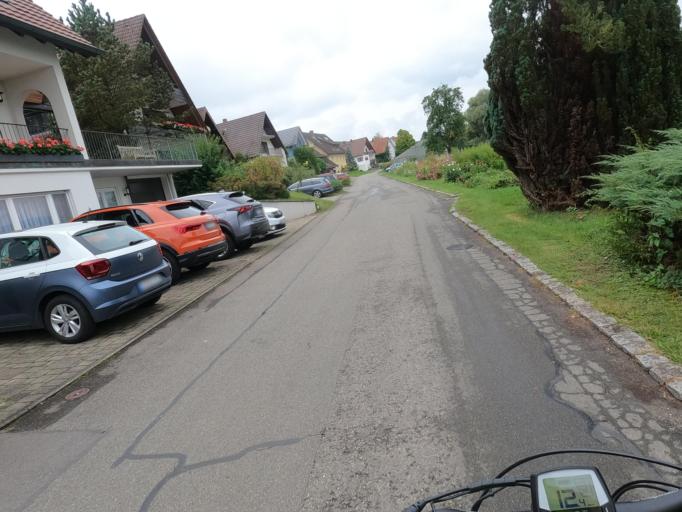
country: DE
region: Baden-Wuerttemberg
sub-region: Freiburg Region
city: Reichenau
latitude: 47.6950
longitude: 9.0752
